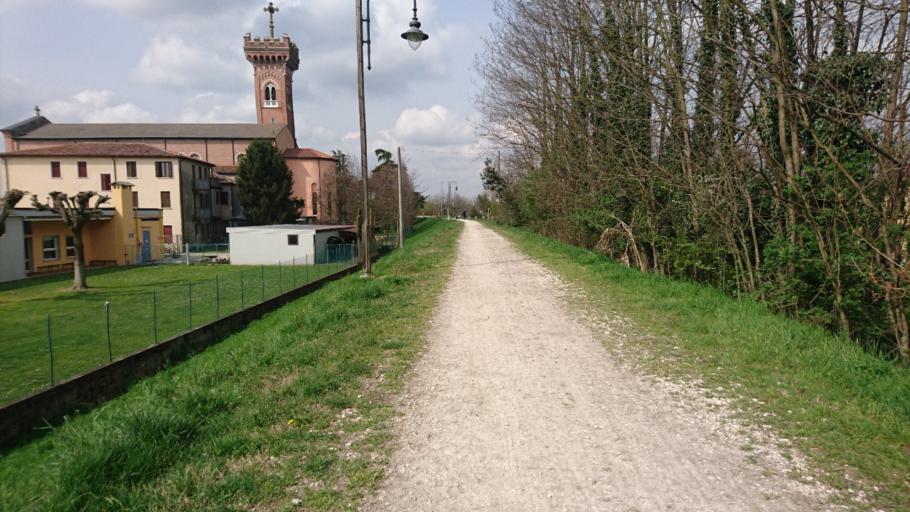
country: IT
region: Veneto
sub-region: Provincia di Padova
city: Limena
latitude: 45.4759
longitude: 11.8491
